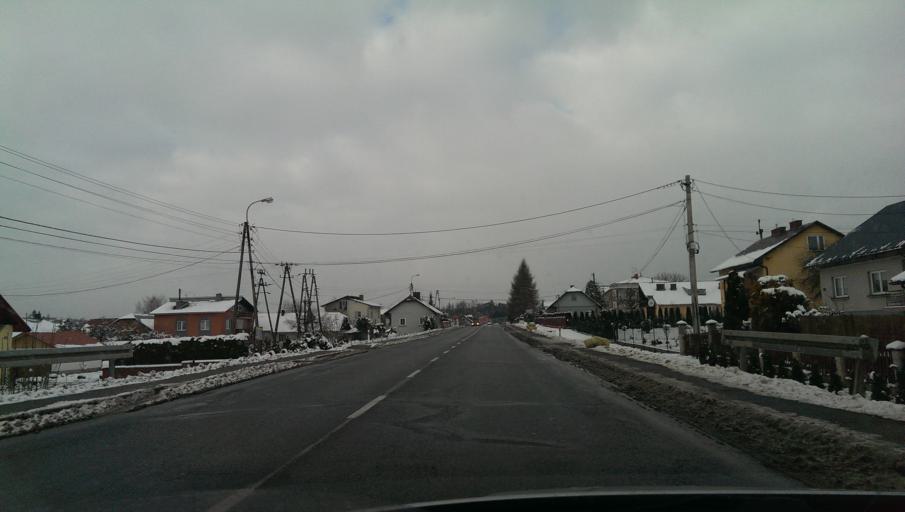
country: PL
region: Subcarpathian Voivodeship
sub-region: Powiat brzozowski
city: Humniska
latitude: 49.6815
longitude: 22.0433
